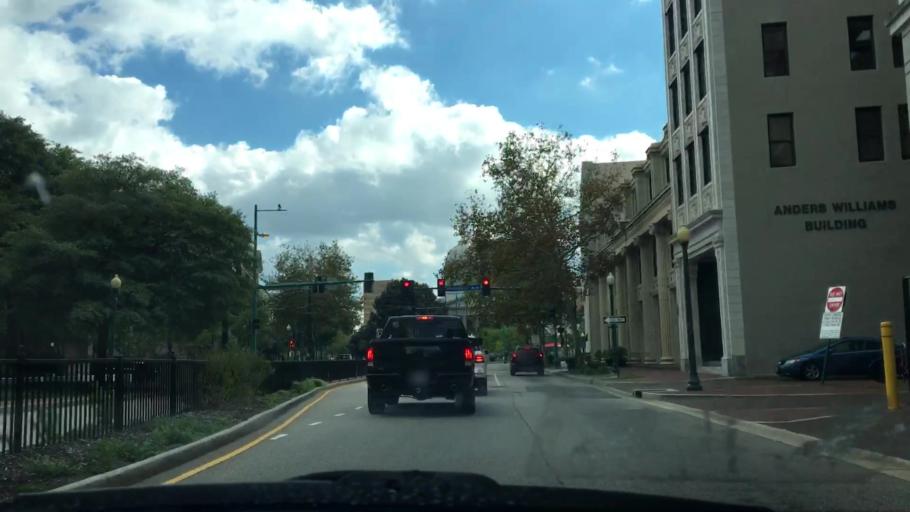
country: US
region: Virginia
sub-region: City of Norfolk
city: Norfolk
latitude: 36.8479
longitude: -76.2912
